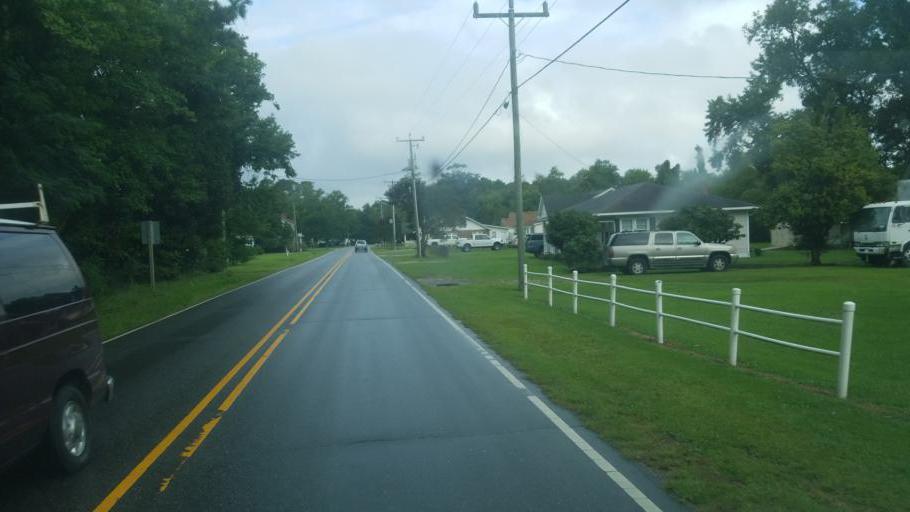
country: US
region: North Carolina
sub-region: Dare County
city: Wanchese
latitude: 35.8443
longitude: -75.6344
